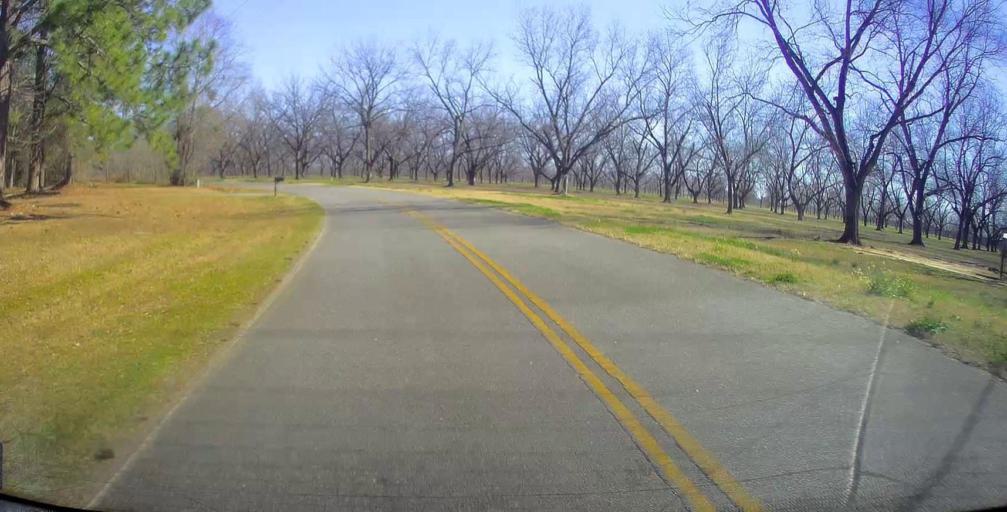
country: US
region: Georgia
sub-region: Peach County
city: Fort Valley
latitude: 32.6298
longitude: -83.8485
